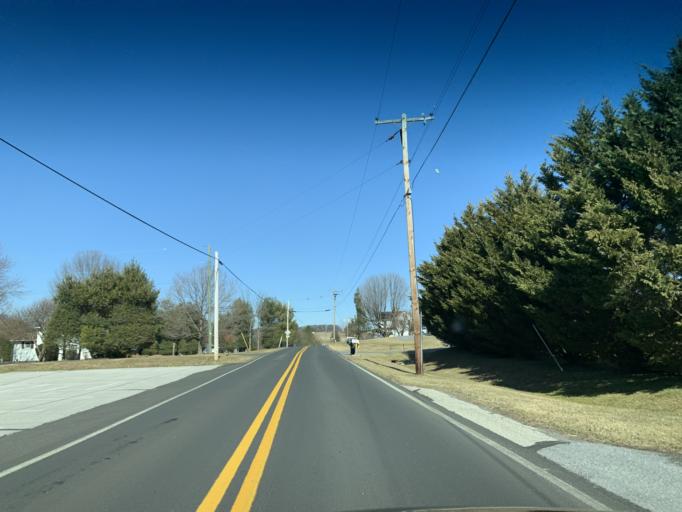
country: US
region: Maryland
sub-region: Carroll County
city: Manchester
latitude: 39.6202
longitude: -76.8941
